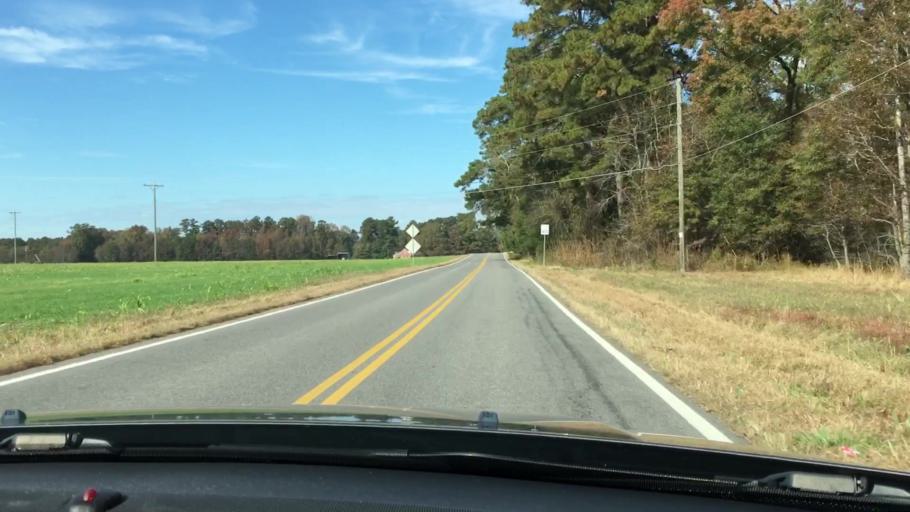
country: US
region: Virginia
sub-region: King William County
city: West Point
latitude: 37.5136
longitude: -76.8203
